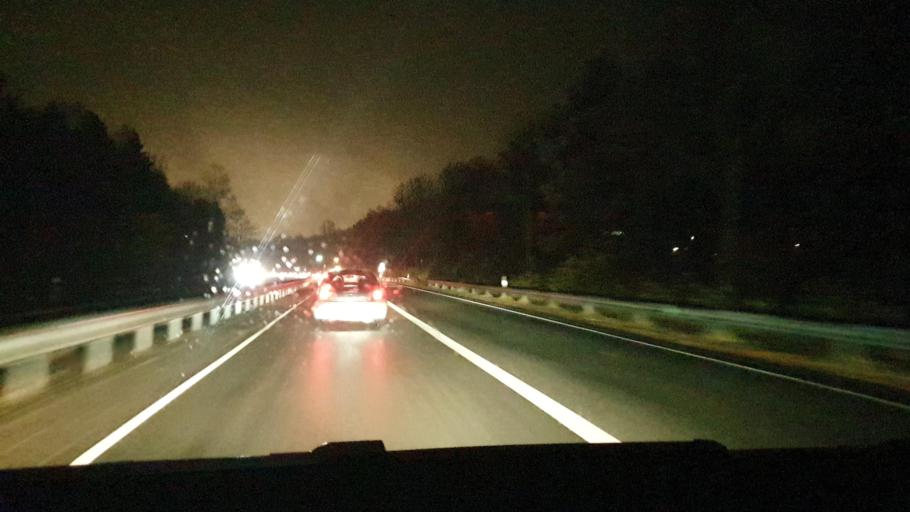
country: DE
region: North Rhine-Westphalia
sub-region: Regierungsbezirk Arnsberg
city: Siegen
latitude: 50.8874
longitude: 7.9969
